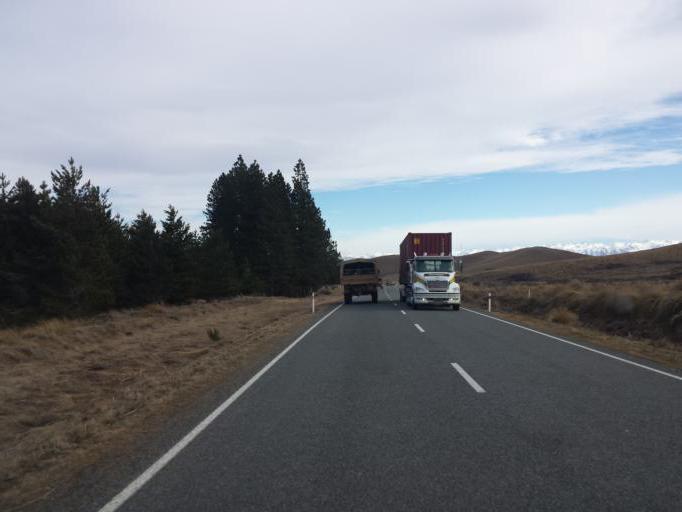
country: NZ
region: Canterbury
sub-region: Timaru District
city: Pleasant Point
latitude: -44.0906
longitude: 170.5887
